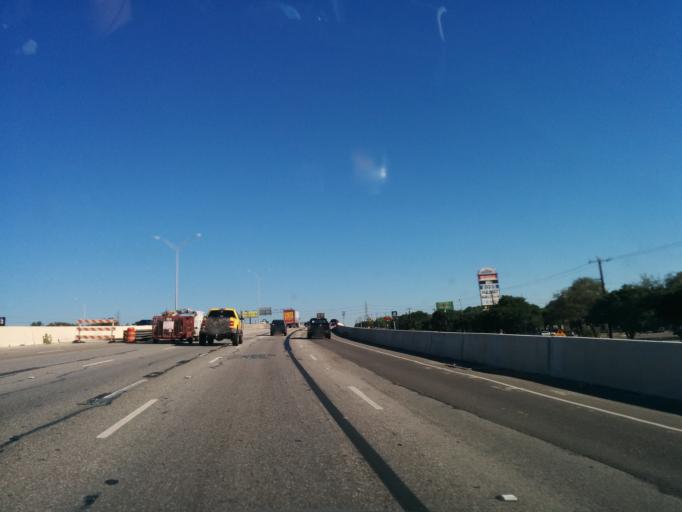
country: US
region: Texas
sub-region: Bexar County
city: Shavano Park
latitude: 29.5488
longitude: -98.5842
